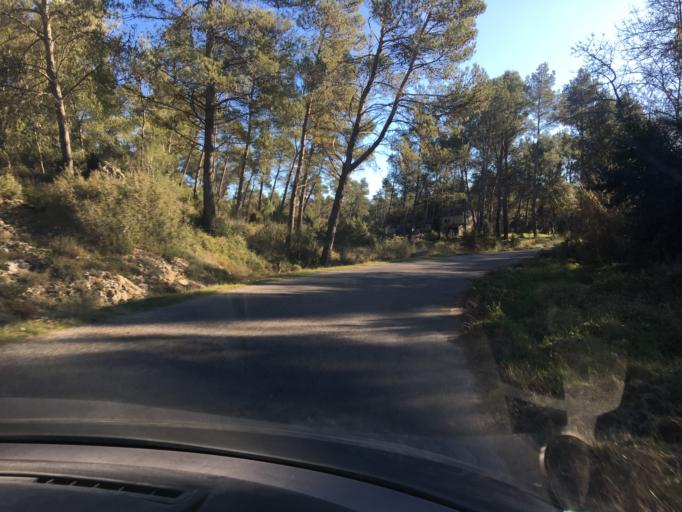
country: FR
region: Provence-Alpes-Cote d'Azur
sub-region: Departement des Bouches-du-Rhone
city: Saint-Remy-de-Provence
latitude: 43.7757
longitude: 4.7931
